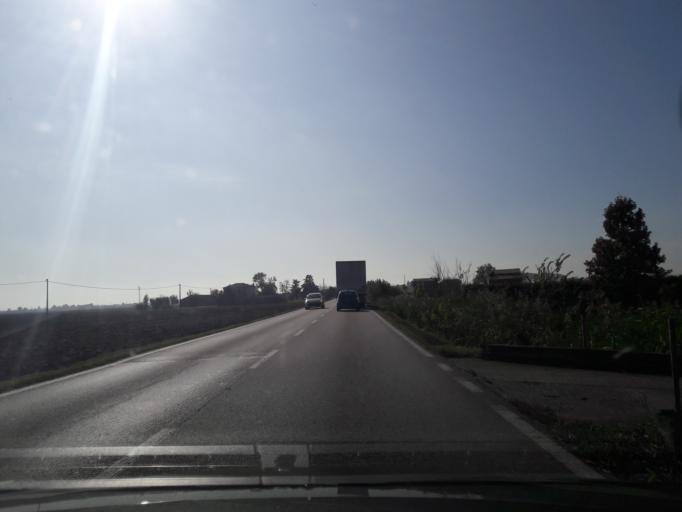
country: IT
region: Veneto
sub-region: Provincia di Rovigo
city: Adria
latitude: 45.0917
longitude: 12.0570
